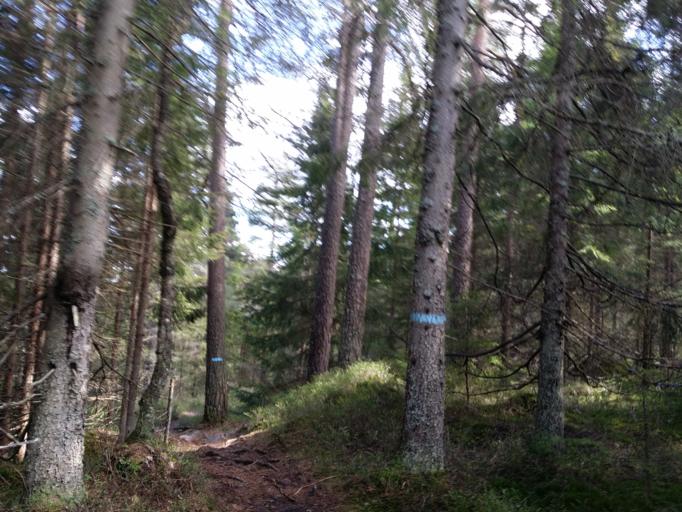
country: NO
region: Oslo
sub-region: Oslo
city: Sjolyststranda
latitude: 59.9892
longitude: 10.7061
